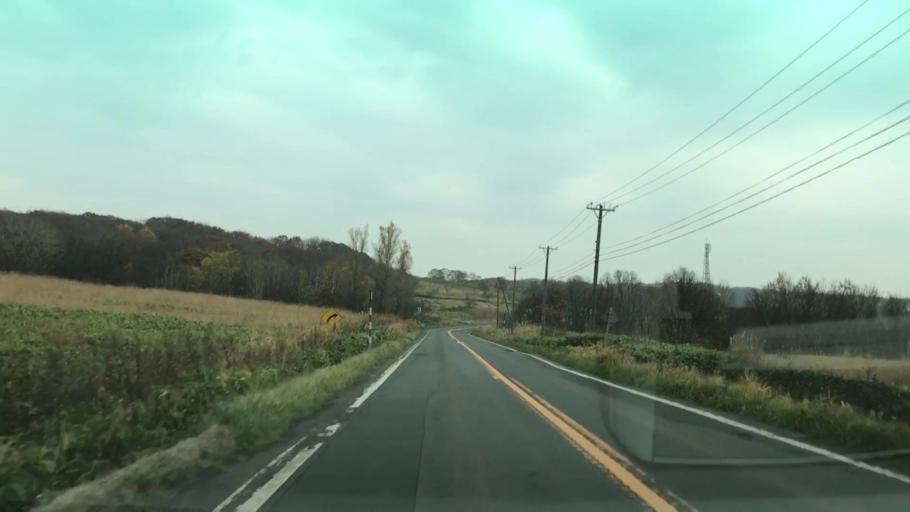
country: JP
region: Hokkaido
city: Ishikari
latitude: 43.3645
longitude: 141.4289
